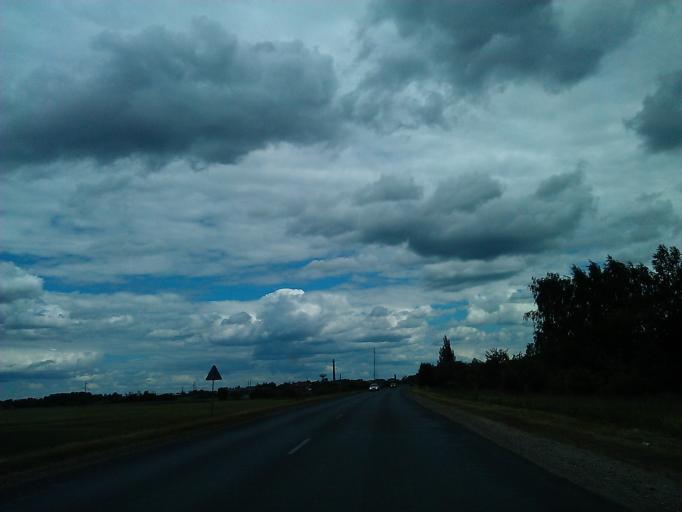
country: LV
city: Tervete
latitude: 56.6217
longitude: 23.4287
